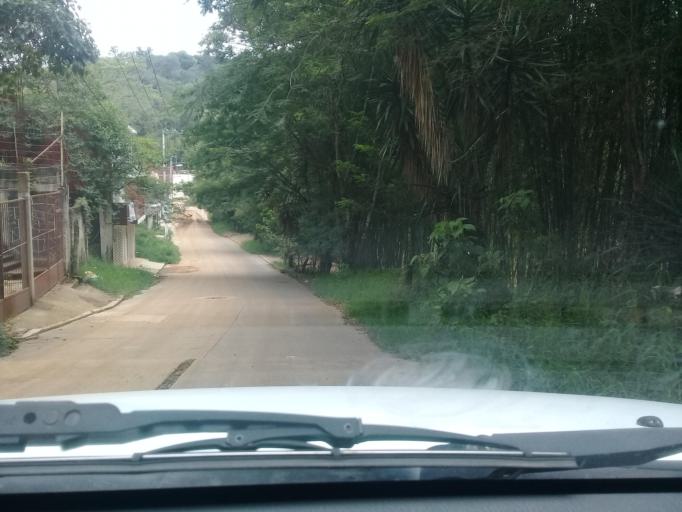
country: MX
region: Veracruz
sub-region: Xalapa
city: Lomas Verdes
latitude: 19.5056
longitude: -96.9140
